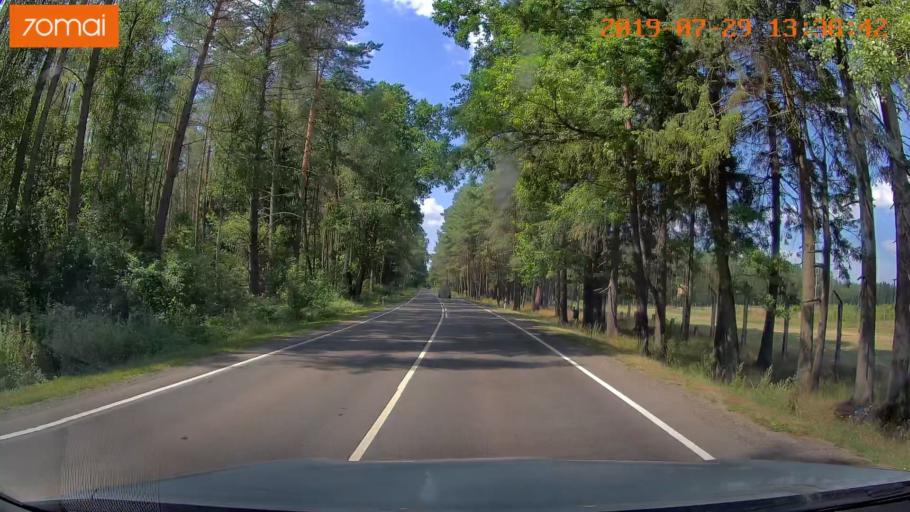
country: RU
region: Kaliningrad
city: Volochayevskoye
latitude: 54.7224
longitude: 20.1670
